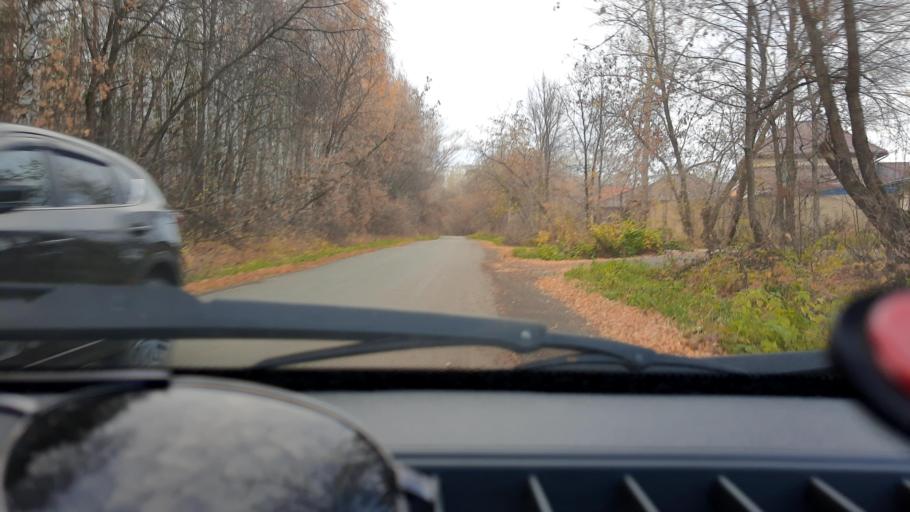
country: RU
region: Bashkortostan
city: Ufa
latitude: 54.7902
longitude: 56.1580
